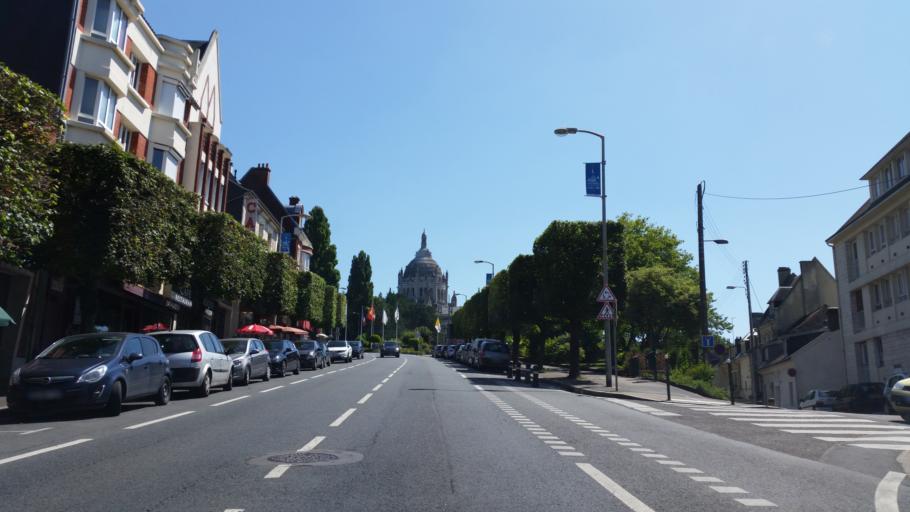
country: FR
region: Lower Normandy
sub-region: Departement du Calvados
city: Lisieux
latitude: 49.1420
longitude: 0.2321
